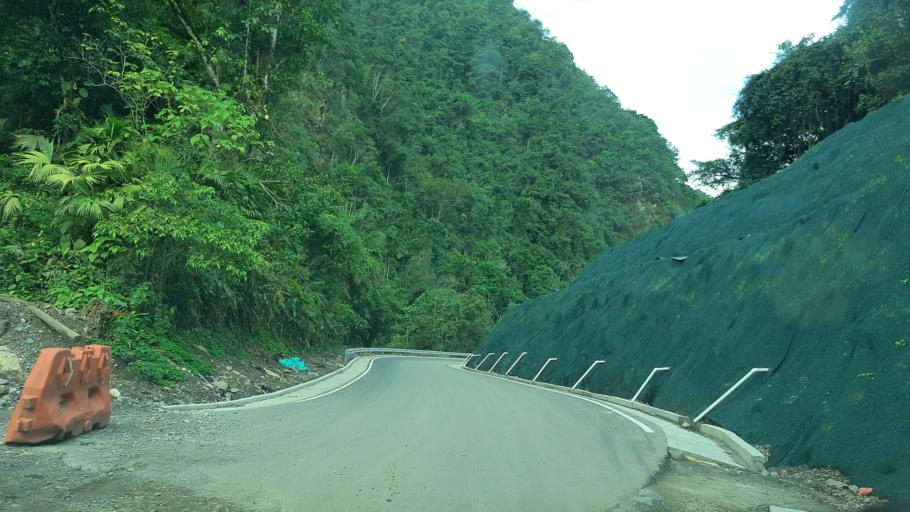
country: CO
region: Boyaca
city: Santa Maria
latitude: 4.8534
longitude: -73.2315
